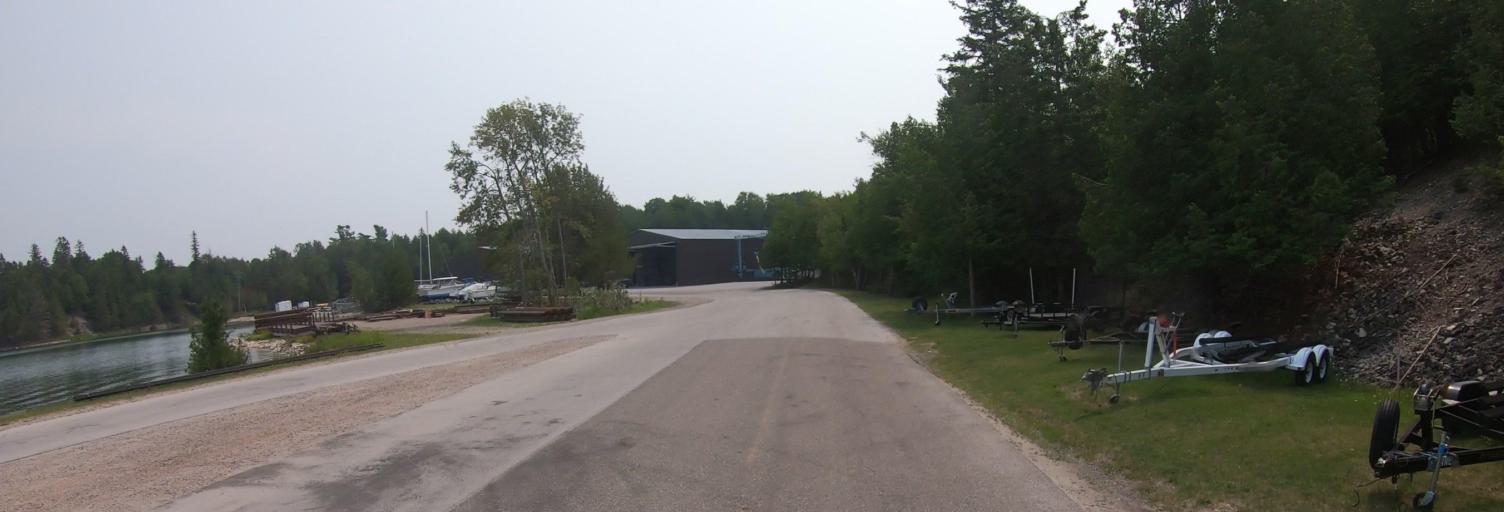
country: CA
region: Ontario
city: Thessalon
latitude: 46.0242
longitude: -83.7506
